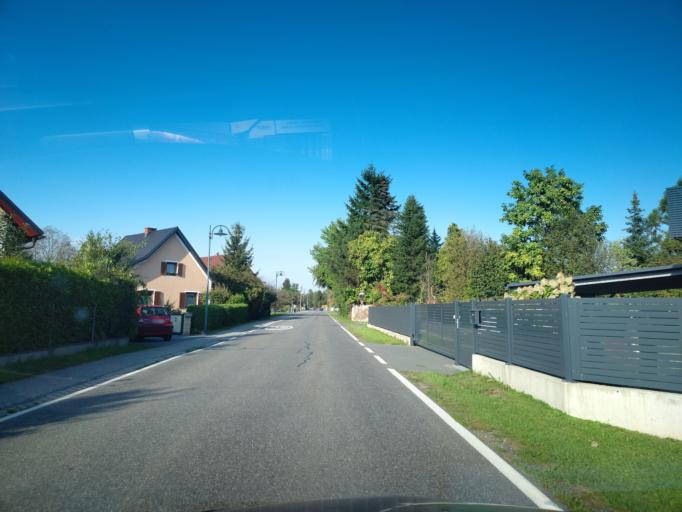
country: AT
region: Styria
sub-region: Politischer Bezirk Leibnitz
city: Kaindorf an der Sulm
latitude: 46.8068
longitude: 15.5447
